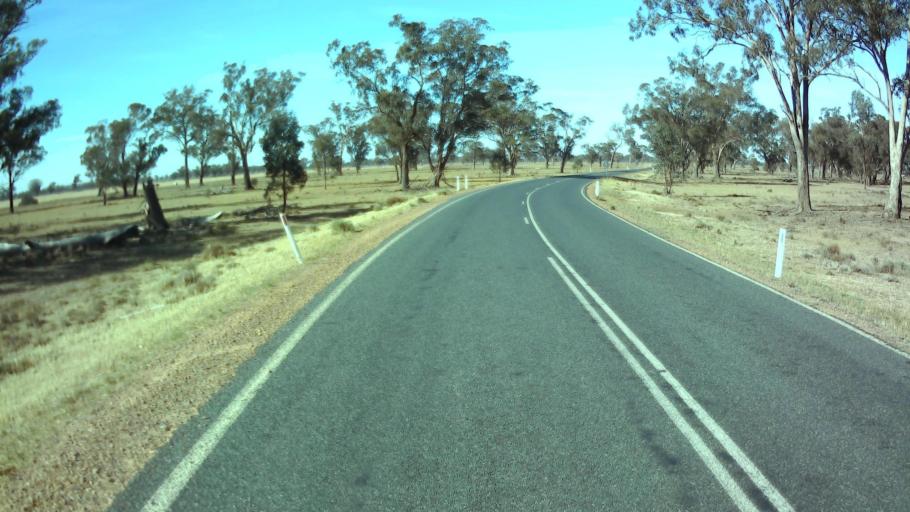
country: AU
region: New South Wales
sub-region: Weddin
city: Grenfell
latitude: -34.0421
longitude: 147.9288
